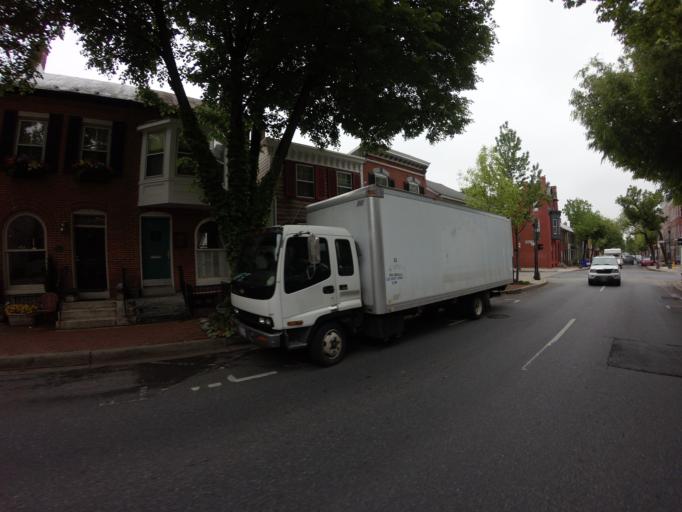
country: US
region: Maryland
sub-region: Frederick County
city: Frederick
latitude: 39.4206
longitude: -77.4101
